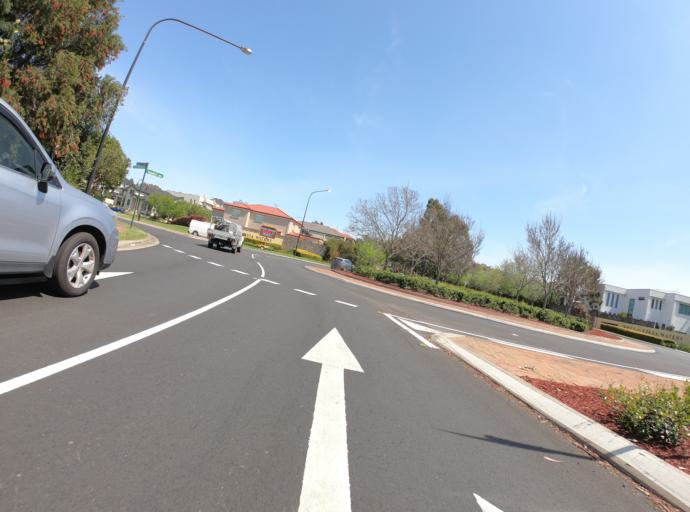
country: AU
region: New South Wales
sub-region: Blacktown
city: Stanhope Gardens
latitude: -33.7375
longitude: 150.9560
